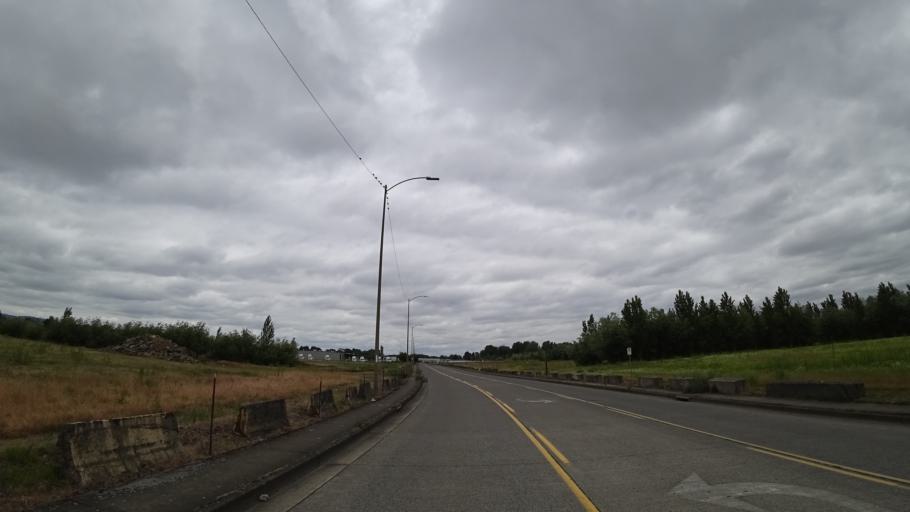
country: US
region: Washington
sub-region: Clark County
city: Vancouver
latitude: 45.5876
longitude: -122.6528
